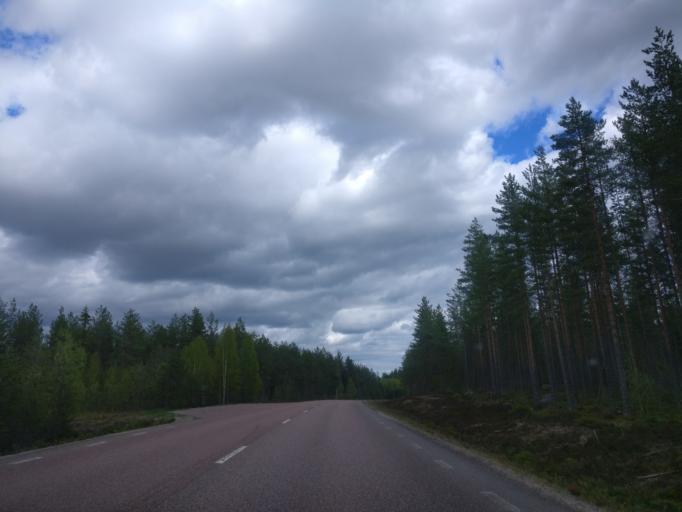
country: SE
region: Gaevleborg
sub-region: Soderhamns Kommun
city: Soderhamn
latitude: 61.4282
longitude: 16.9768
